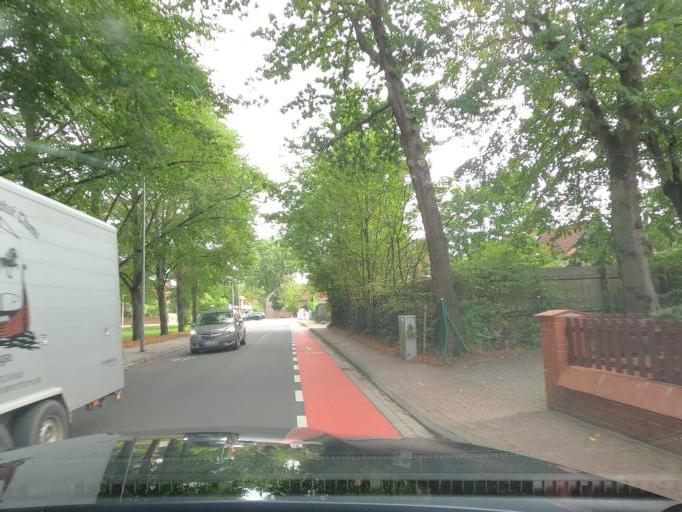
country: DE
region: Lower Saxony
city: Isernhagen Farster Bauerschaft
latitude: 52.5117
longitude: 9.9195
